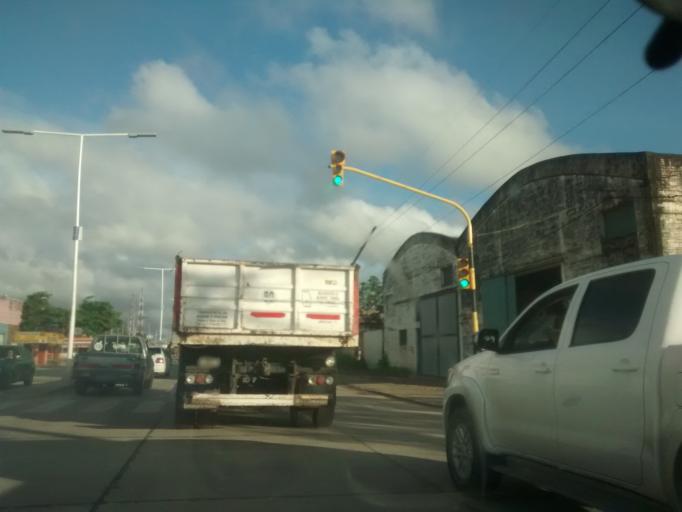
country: AR
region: Chaco
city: Fontana
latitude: -27.4369
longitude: -59.0171
